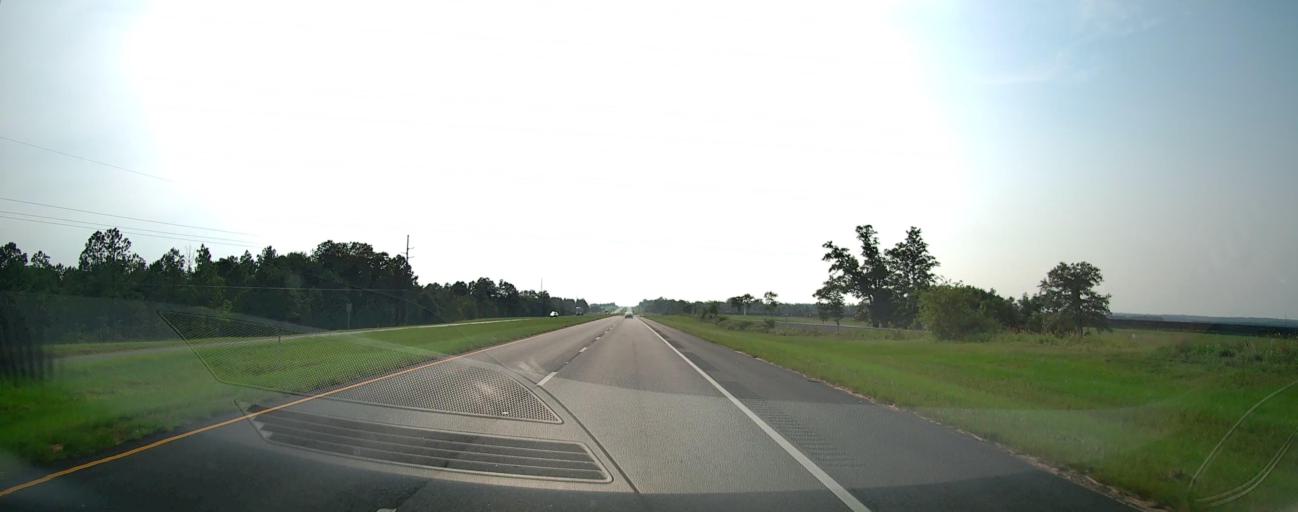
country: US
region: Georgia
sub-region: Taylor County
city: Butler
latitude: 32.5733
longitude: -84.2947
